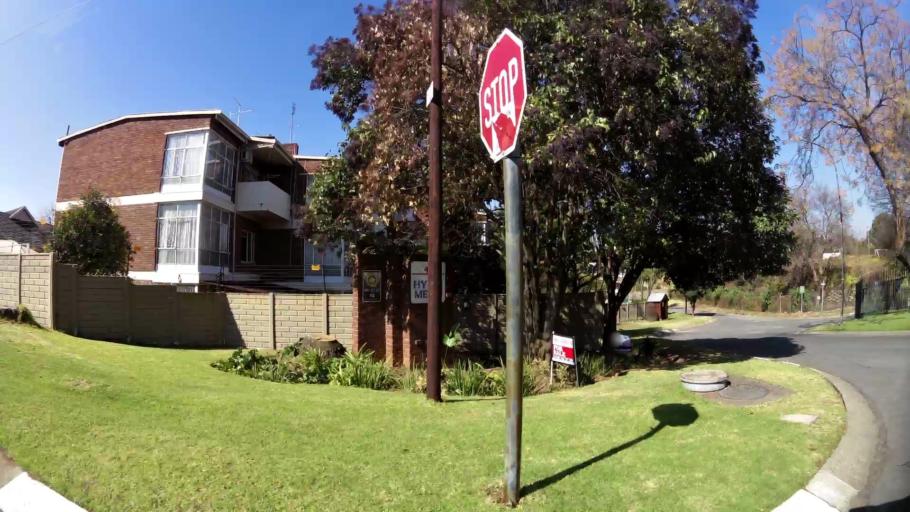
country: ZA
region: Gauteng
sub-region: City of Johannesburg Metropolitan Municipality
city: Johannesburg
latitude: -26.1456
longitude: 28.1024
